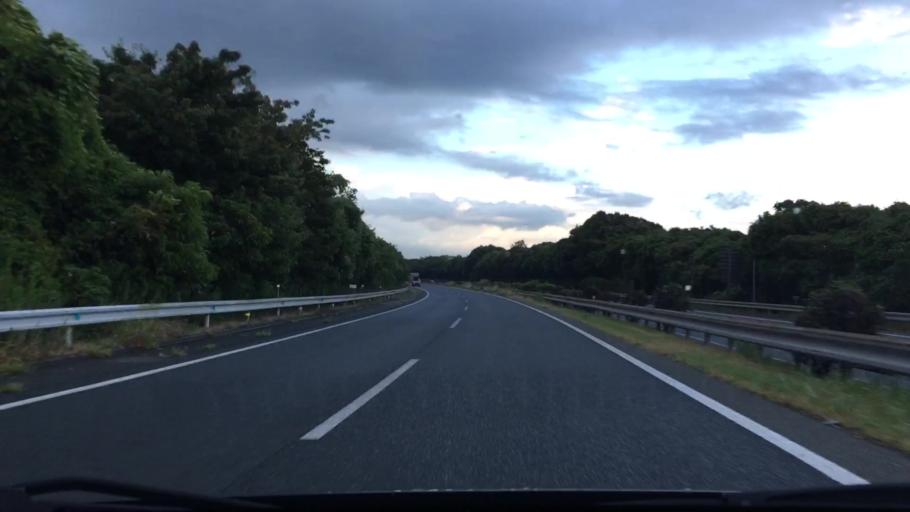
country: JP
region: Yamaguchi
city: Shimonoseki
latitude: 33.8751
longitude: 130.9680
